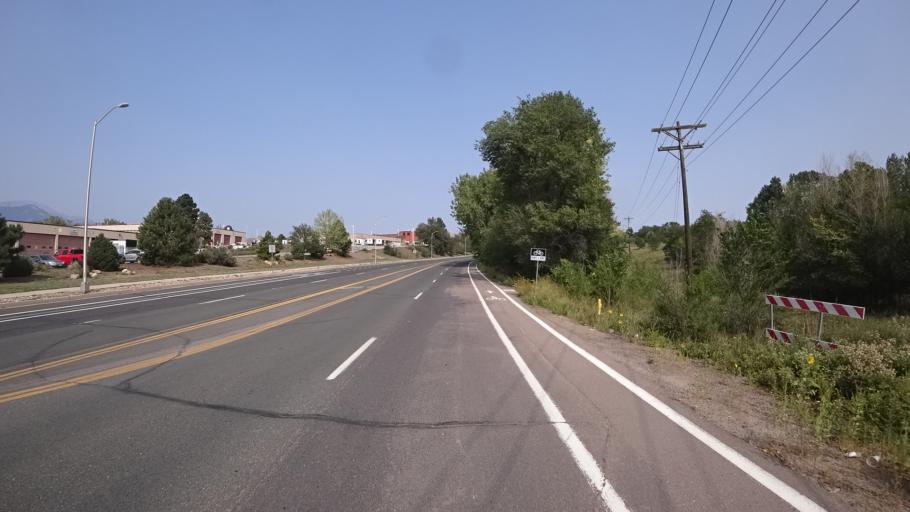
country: US
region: Colorado
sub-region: El Paso County
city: Colorado Springs
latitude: 38.8145
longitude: -104.8038
